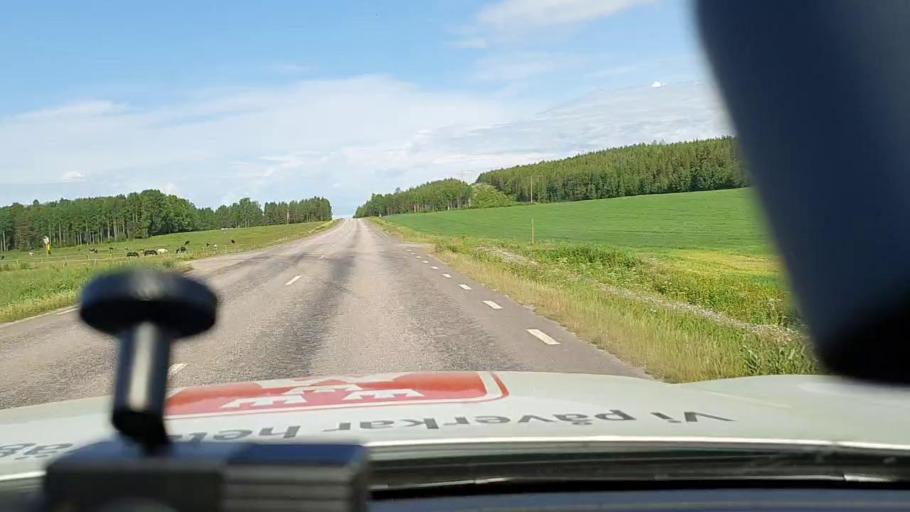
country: SE
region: Norrbotten
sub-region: Bodens Kommun
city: Boden
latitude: 65.9122
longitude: 21.3461
